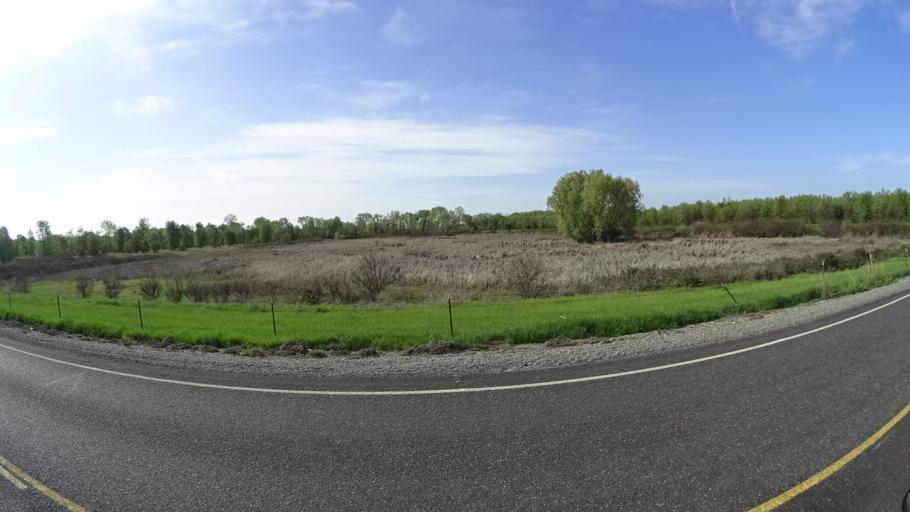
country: US
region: California
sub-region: Glenn County
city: Hamilton City
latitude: 39.6308
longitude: -122.0013
